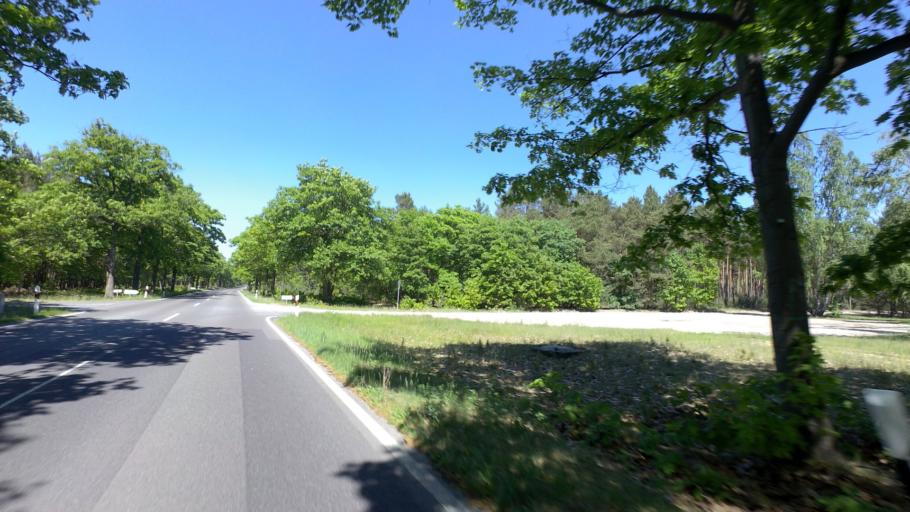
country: DE
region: Brandenburg
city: Drachhausen
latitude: 51.9209
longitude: 14.3484
